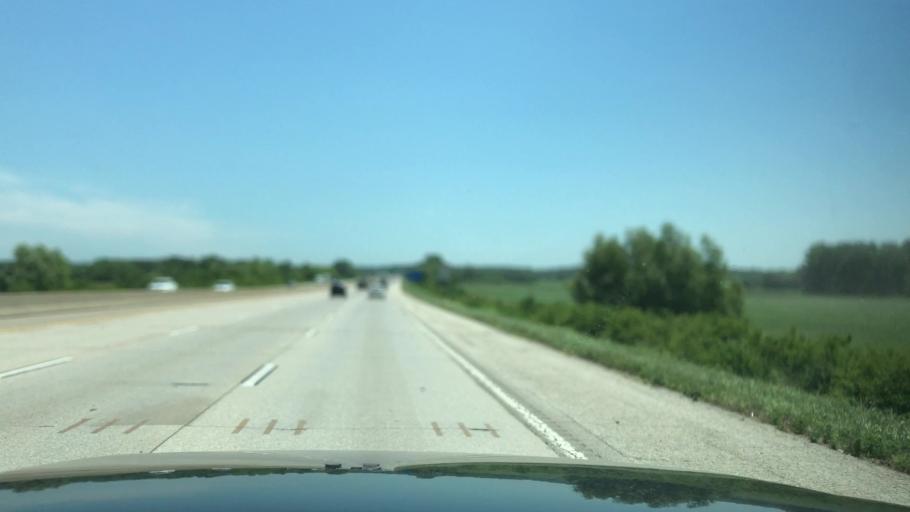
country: US
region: Missouri
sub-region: Saint Louis County
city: Bridgeton
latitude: 38.7914
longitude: -90.4424
